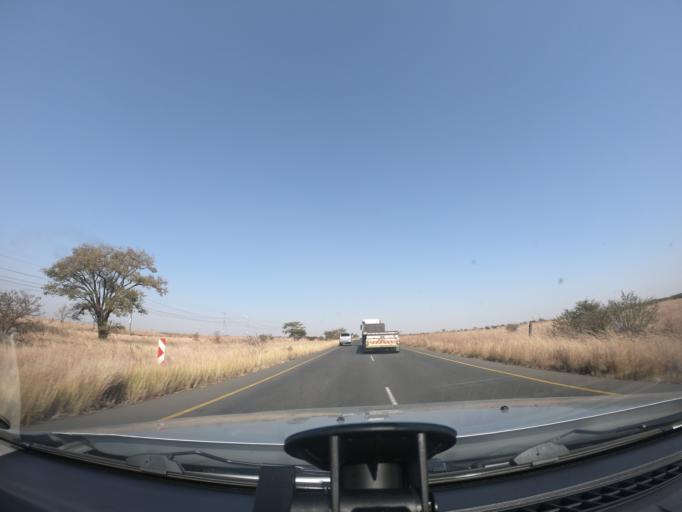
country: ZA
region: KwaZulu-Natal
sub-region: uThukela District Municipality
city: Ladysmith
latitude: -28.7599
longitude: 29.8202
